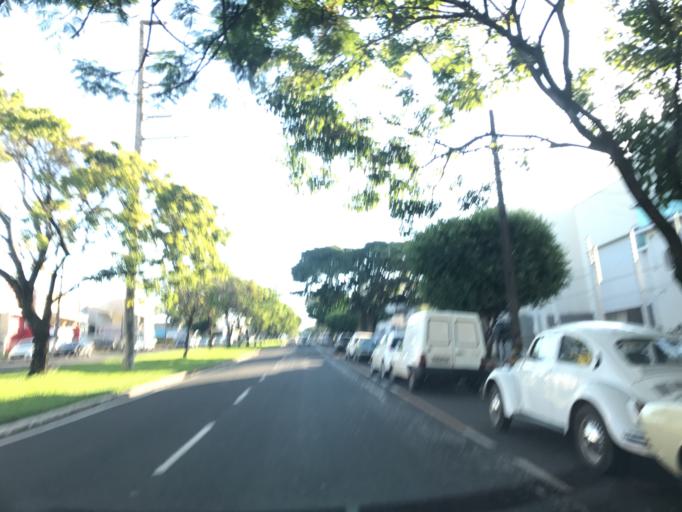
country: BR
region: Parana
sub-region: Maringa
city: Maringa
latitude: -23.4483
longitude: -51.9455
